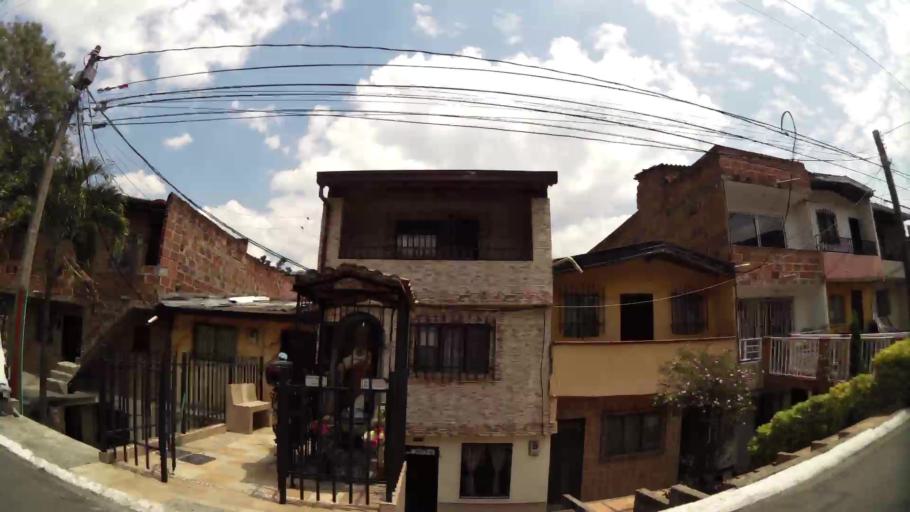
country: CO
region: Antioquia
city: Medellin
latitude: 6.2941
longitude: -75.5703
